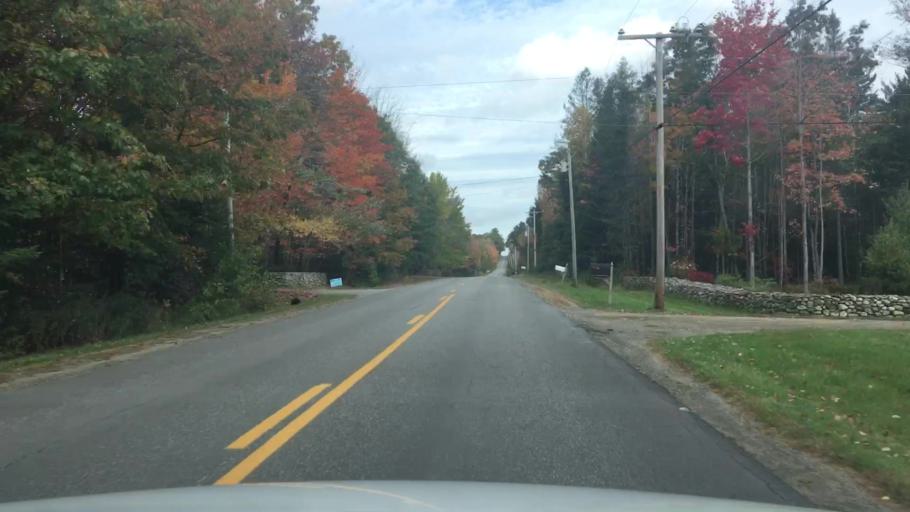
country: US
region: Maine
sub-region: Waldo County
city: Searsmont
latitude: 44.3836
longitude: -69.1321
